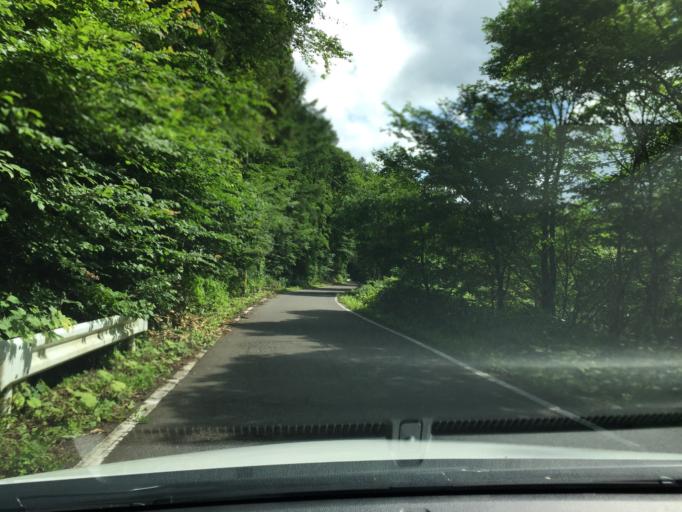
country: JP
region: Fukushima
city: Inawashiro
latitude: 37.2856
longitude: 140.0640
